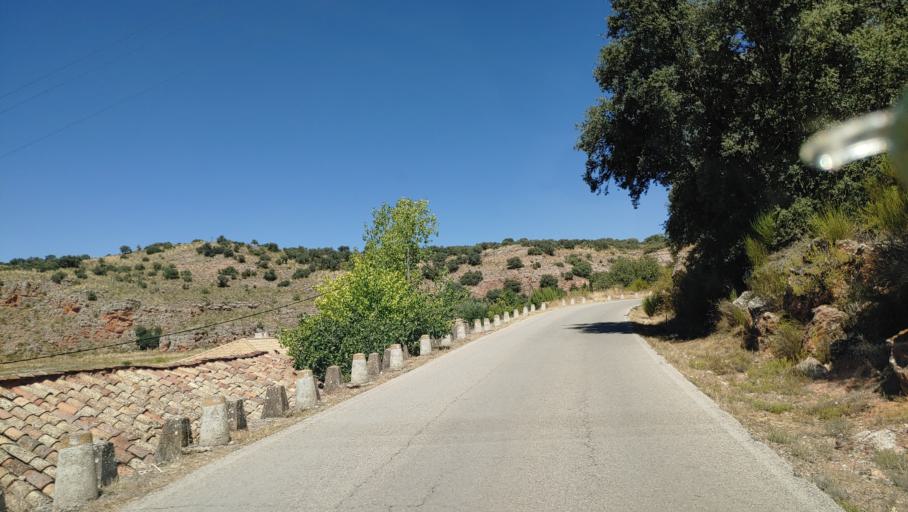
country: ES
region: Castille-La Mancha
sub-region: Provincia de Ciudad Real
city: Ruidera
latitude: 38.9255
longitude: -2.8327
